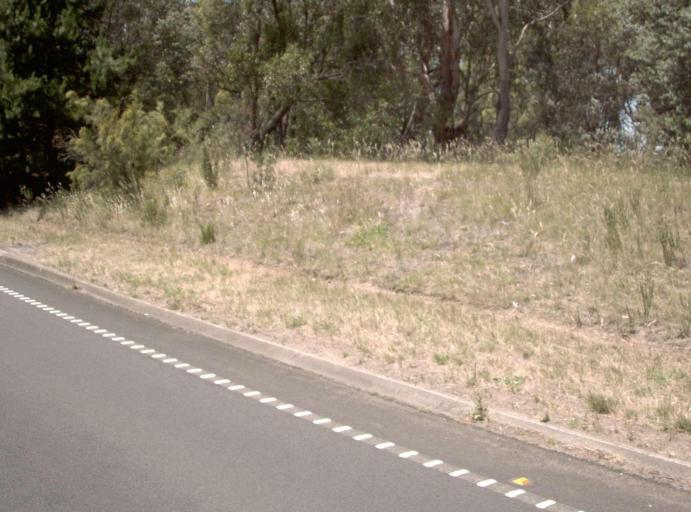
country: AU
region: Victoria
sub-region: Cardinia
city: Garfield
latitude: -38.0783
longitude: 145.6875
